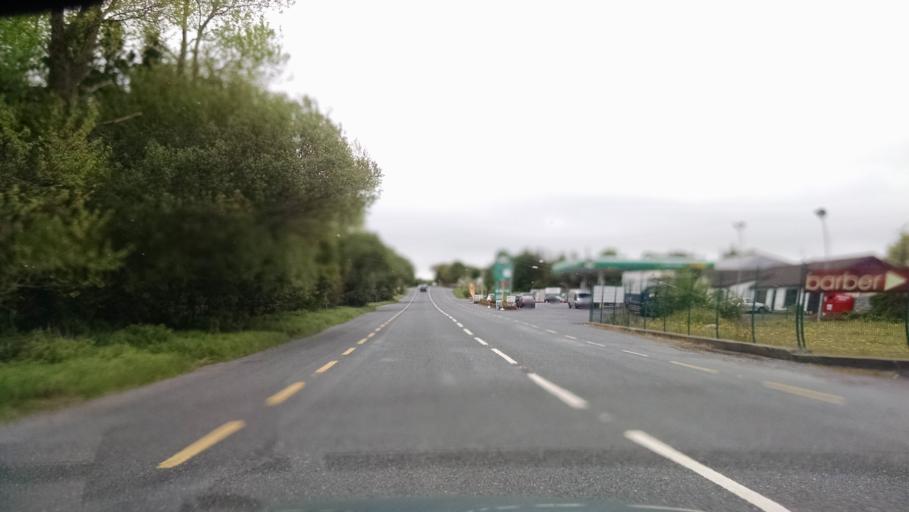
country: IE
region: Connaught
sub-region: County Galway
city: Moycullen
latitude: 53.4508
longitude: -9.0927
